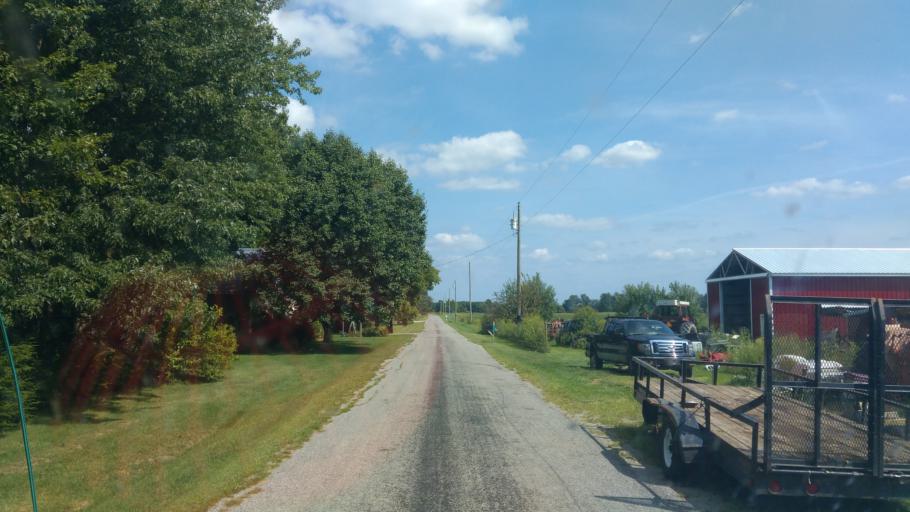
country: US
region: Ohio
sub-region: Union County
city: Richwood
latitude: 40.3981
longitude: -83.4504
